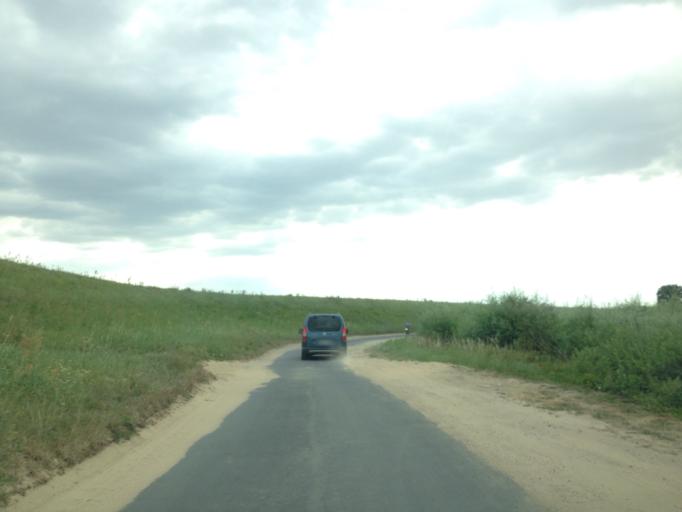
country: PL
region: Kujawsko-Pomorskie
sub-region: Powiat chelminski
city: Chelmno
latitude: 53.3691
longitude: 18.4002
